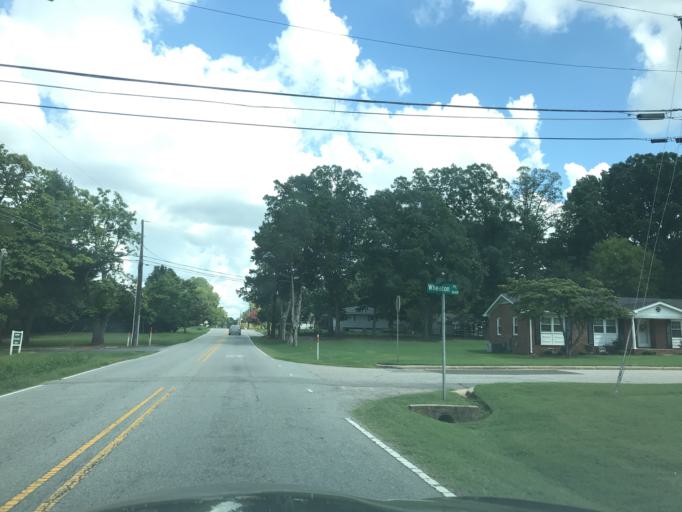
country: US
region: North Carolina
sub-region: Wake County
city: Raleigh
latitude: 35.8320
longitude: -78.6146
